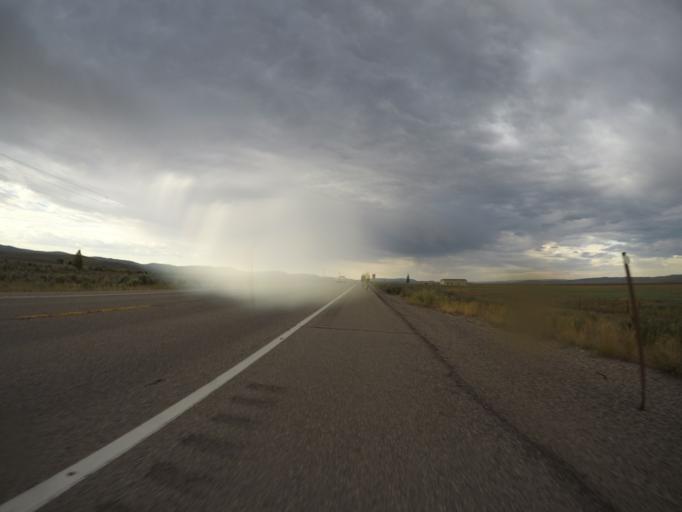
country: US
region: Utah
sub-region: Rich County
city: Randolph
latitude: 41.9358
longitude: -110.9537
